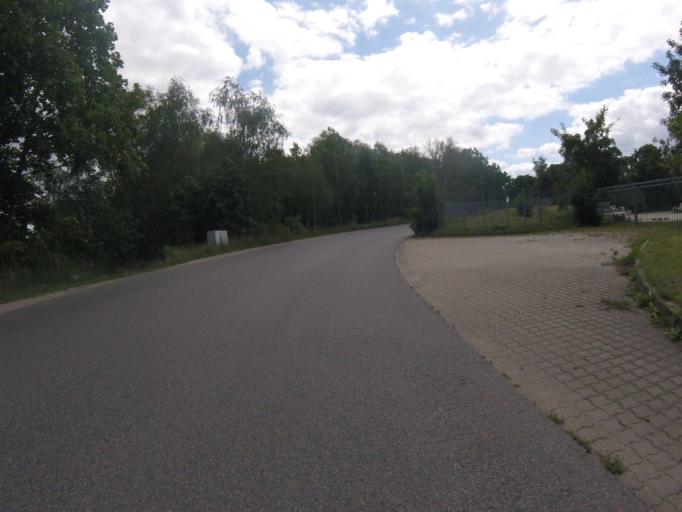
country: DE
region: Brandenburg
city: Mittenwalde
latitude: 52.2526
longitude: 13.5220
